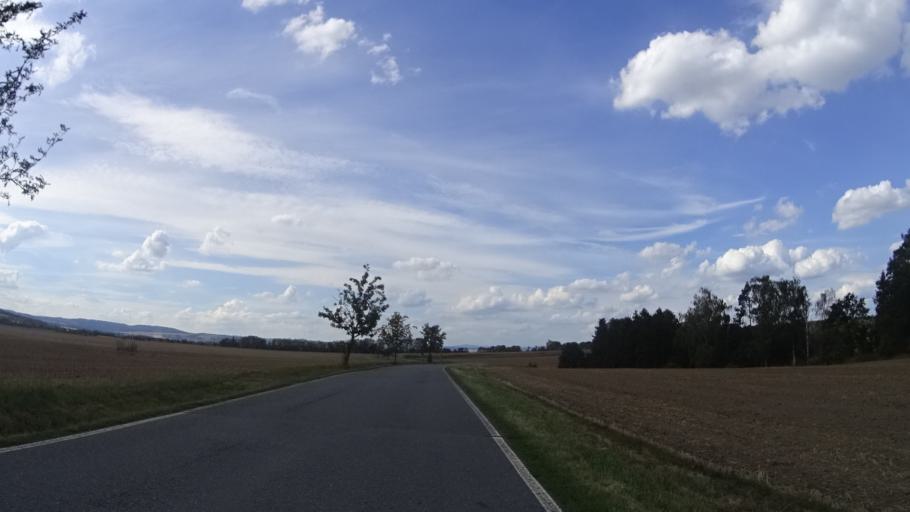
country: CZ
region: Olomoucky
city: Bila Lhota
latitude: 49.7338
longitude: 16.9775
